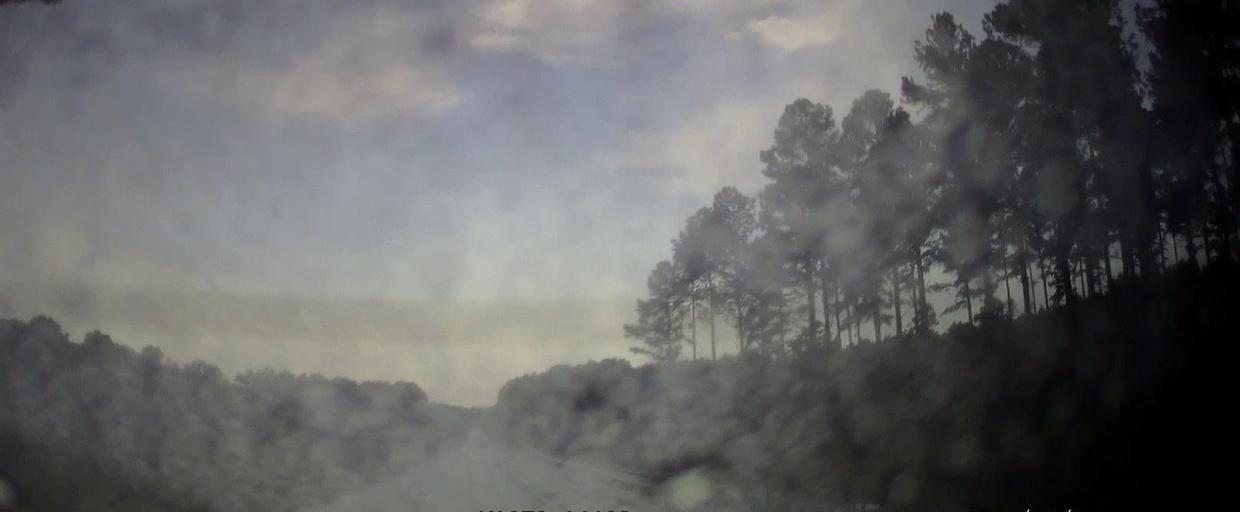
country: US
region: Georgia
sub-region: Dodge County
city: Chester
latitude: 32.5525
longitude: -83.1390
